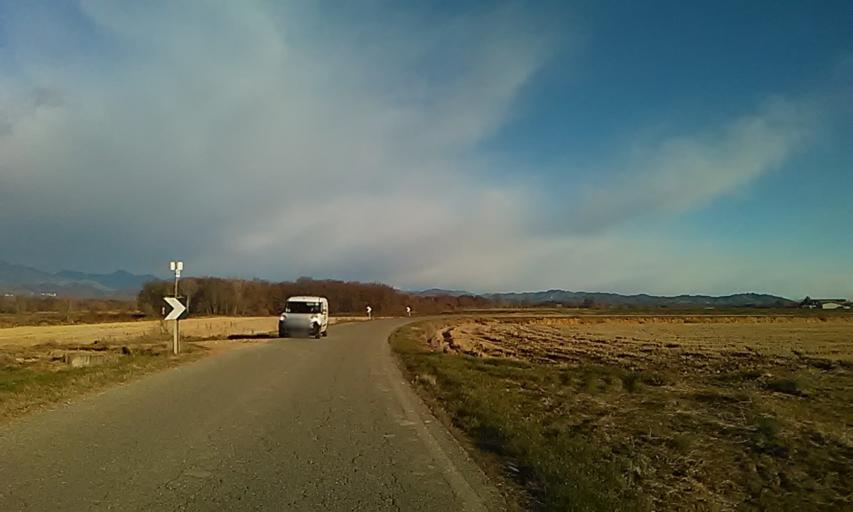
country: IT
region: Piedmont
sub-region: Provincia di Vercelli
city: Rovasenda
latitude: 45.5397
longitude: 8.2736
